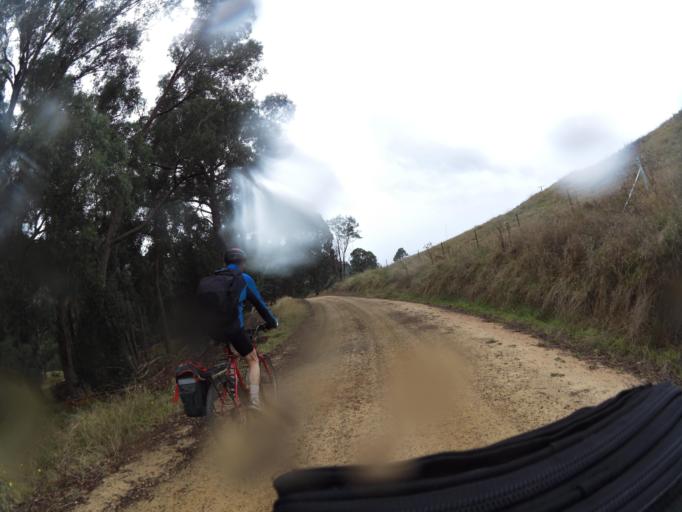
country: AU
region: New South Wales
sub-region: Greater Hume Shire
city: Holbrook
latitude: -36.2375
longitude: 147.6150
